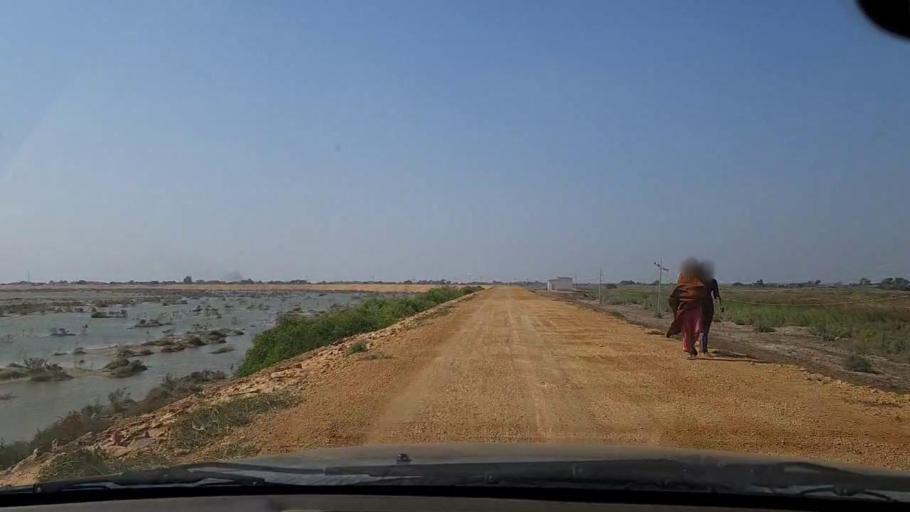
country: PK
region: Sindh
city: Chuhar Jamali
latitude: 24.4563
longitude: 67.8703
